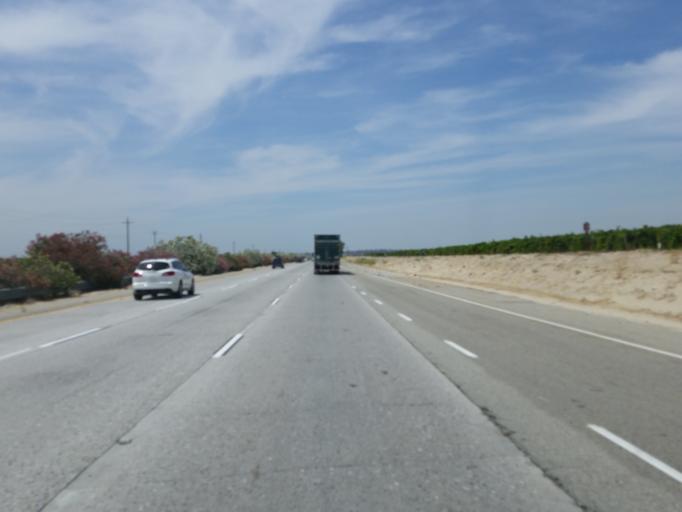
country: US
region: California
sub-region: Kern County
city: Weedpatch
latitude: 35.1266
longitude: -118.9895
